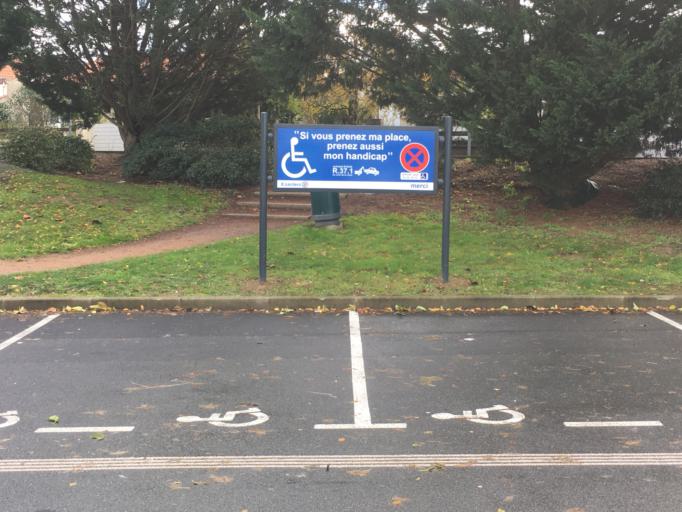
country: FR
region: Pays de la Loire
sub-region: Departement de la Loire-Atlantique
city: Clisson
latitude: 47.0972
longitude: -1.2803
